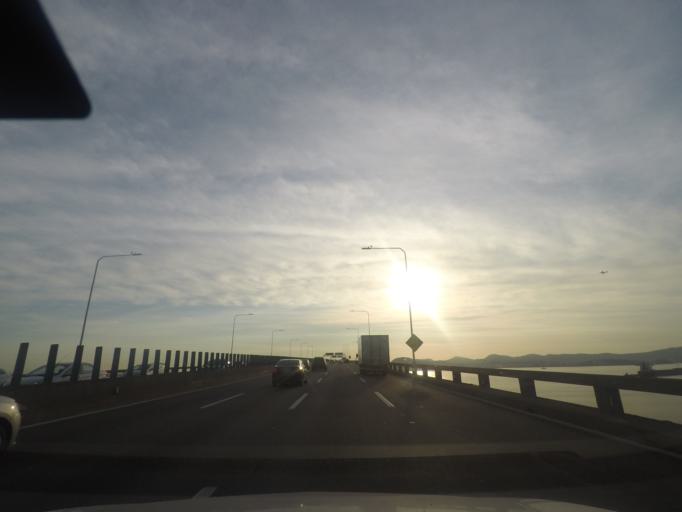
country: BR
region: Rio de Janeiro
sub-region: Rio De Janeiro
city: Rio de Janeiro
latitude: -22.8700
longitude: -43.1709
